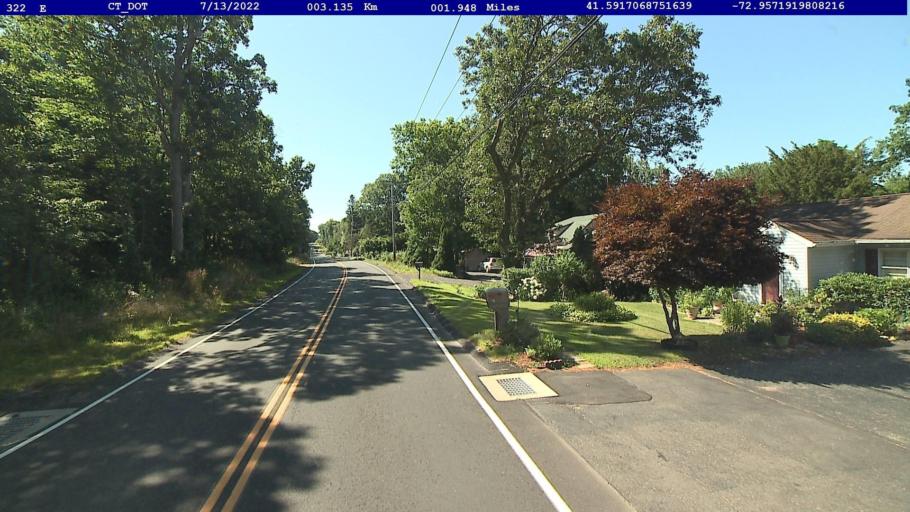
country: US
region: Connecticut
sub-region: New Haven County
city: Wolcott
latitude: 41.5917
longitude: -72.9572
